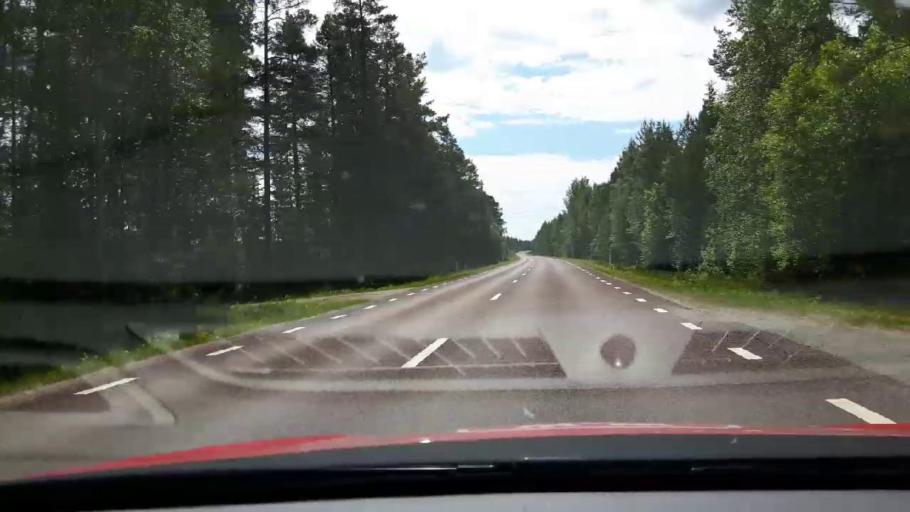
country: SE
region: Jaemtland
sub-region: Harjedalens Kommun
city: Sveg
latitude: 62.1125
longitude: 14.9704
